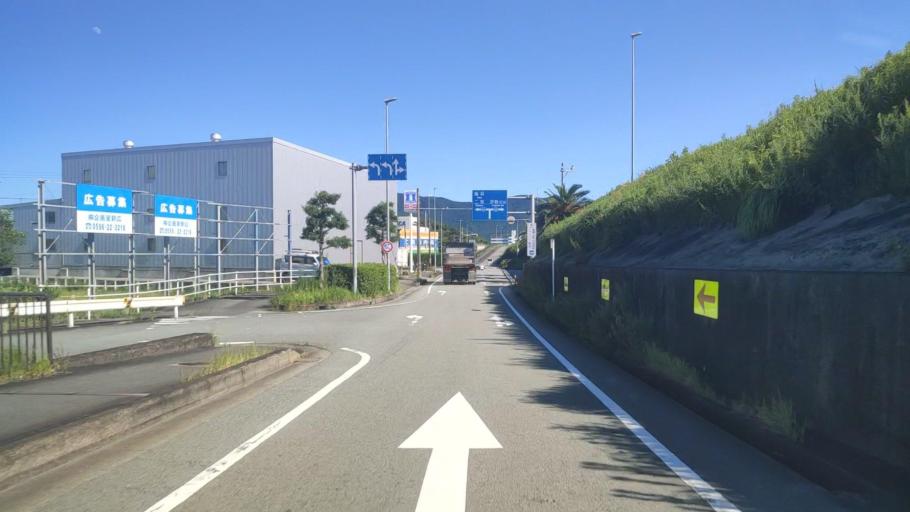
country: JP
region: Mie
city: Ise
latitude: 34.4998
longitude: 136.7399
